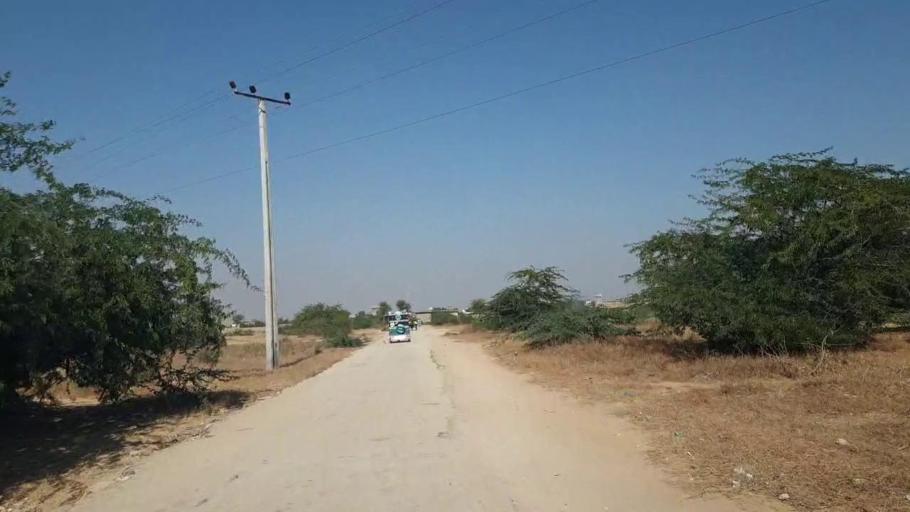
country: PK
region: Sindh
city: Jamshoro
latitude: 25.3540
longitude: 67.8313
